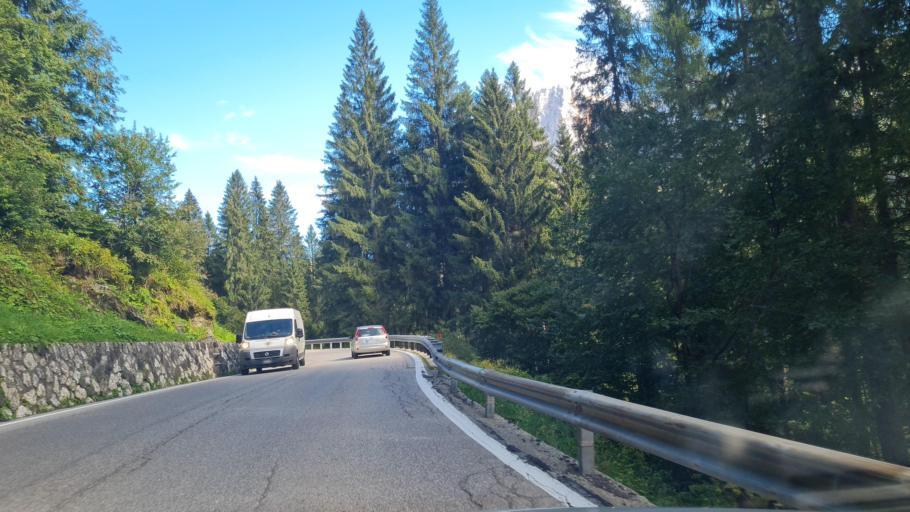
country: IT
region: Trentino-Alto Adige
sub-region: Provincia di Trento
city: Siror
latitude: 46.2479
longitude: 11.8032
